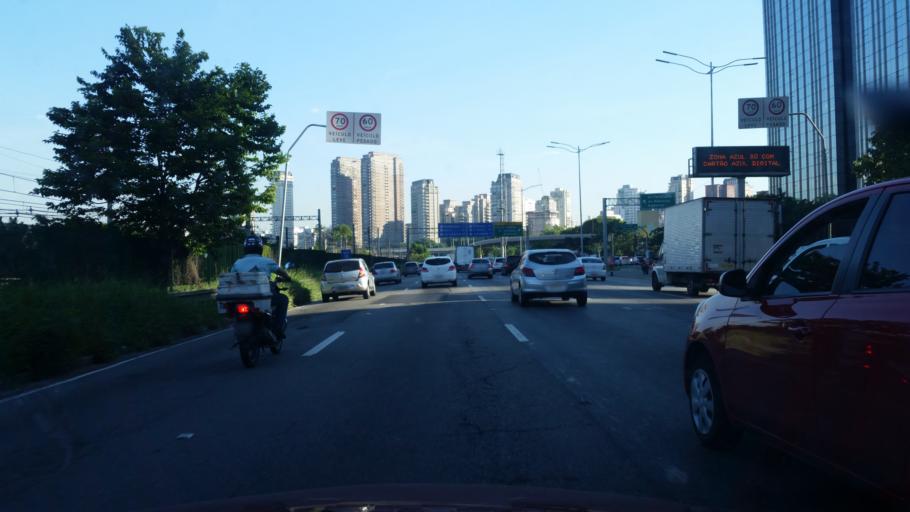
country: BR
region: Sao Paulo
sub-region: Sao Paulo
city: Sao Paulo
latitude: -23.5918
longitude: -46.6920
